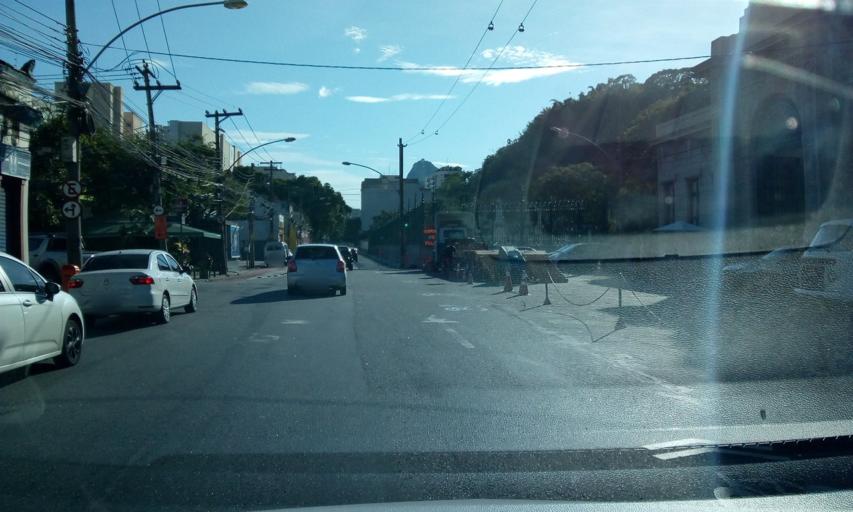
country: BR
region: Rio de Janeiro
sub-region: Rio De Janeiro
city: Rio de Janeiro
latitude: -22.9575
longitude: -43.1896
